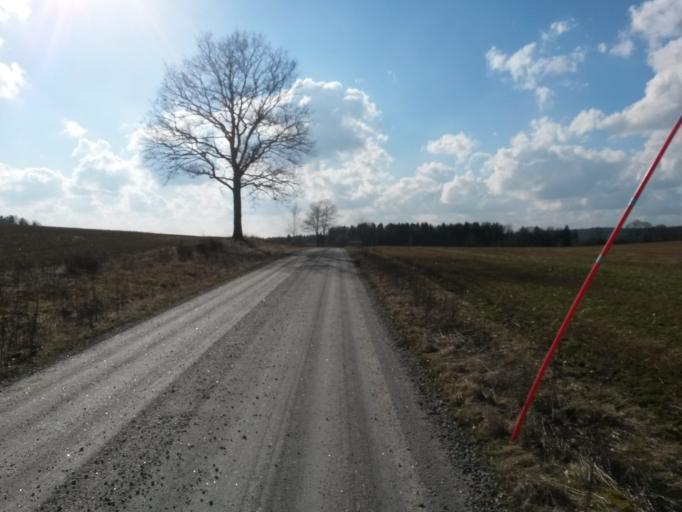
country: SE
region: Vaestra Goetaland
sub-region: Vargarda Kommun
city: Jonstorp
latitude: 57.9897
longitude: 12.6456
